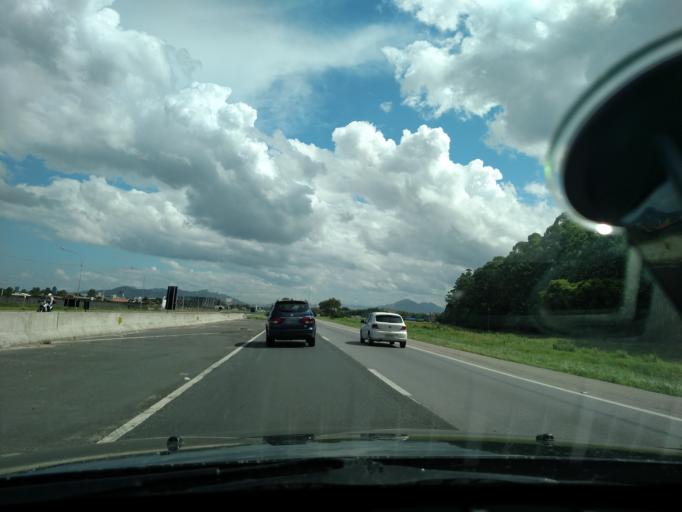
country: BR
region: Santa Catarina
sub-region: Tijucas
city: Tijucas
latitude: -27.2144
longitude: -48.6231
